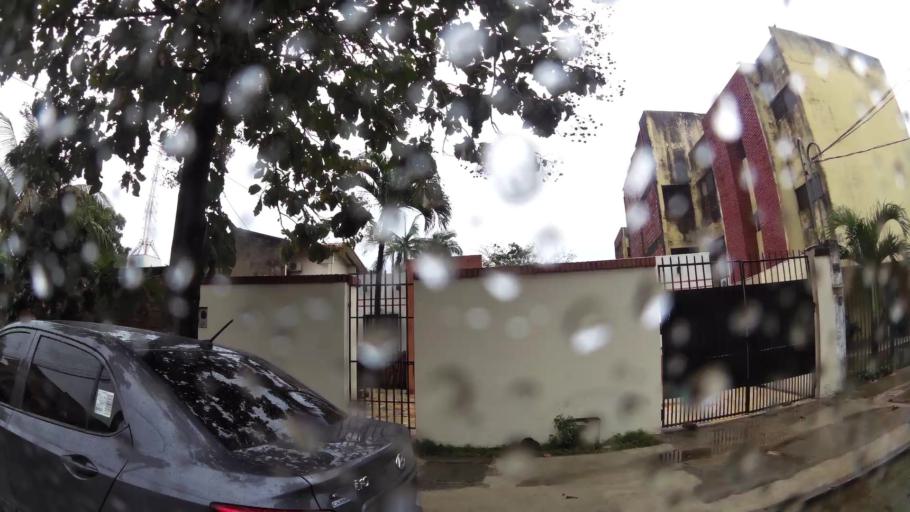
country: BO
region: Santa Cruz
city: Santa Cruz de la Sierra
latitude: -17.7894
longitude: -63.2097
